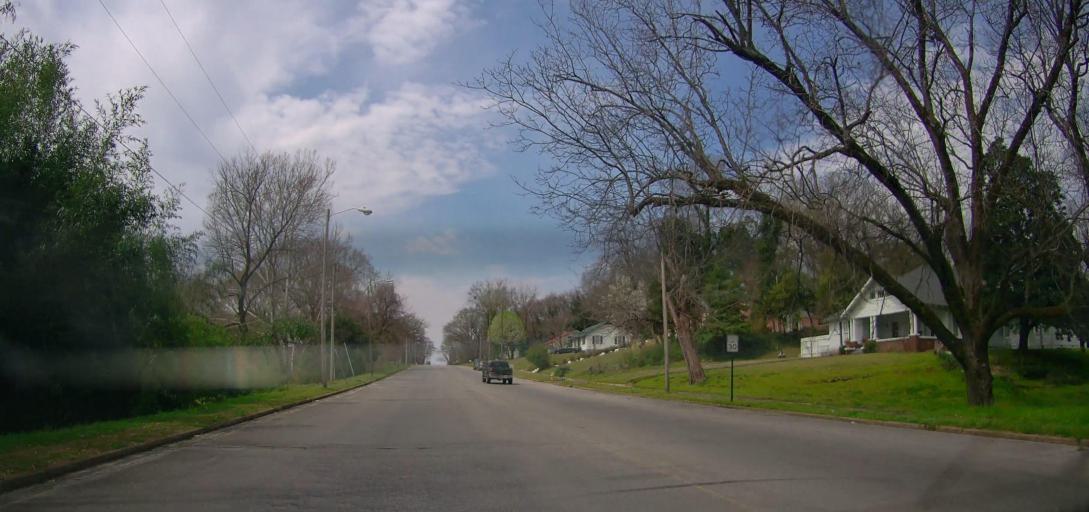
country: US
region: Mississippi
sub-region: Marshall County
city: Holly Springs
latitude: 34.7675
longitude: -89.4389
